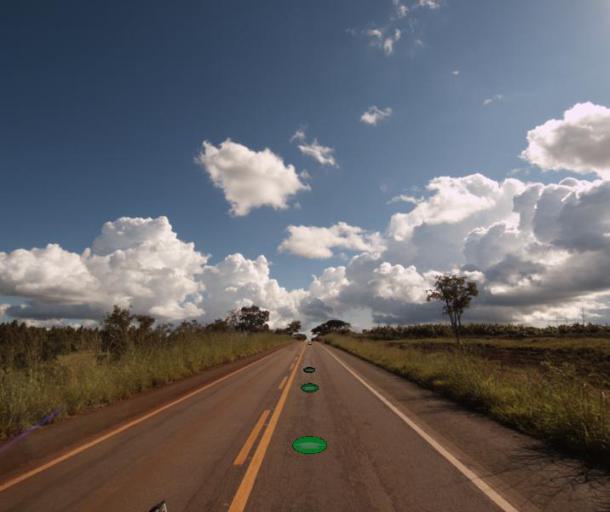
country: BR
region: Goias
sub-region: Itaberai
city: Itaberai
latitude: -15.9435
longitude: -49.6316
